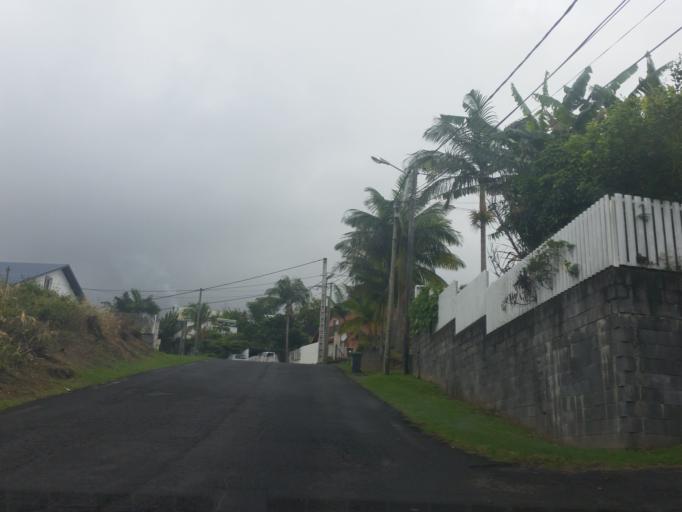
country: RE
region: Reunion
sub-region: Reunion
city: Le Tampon
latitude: -21.2394
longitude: 55.5174
